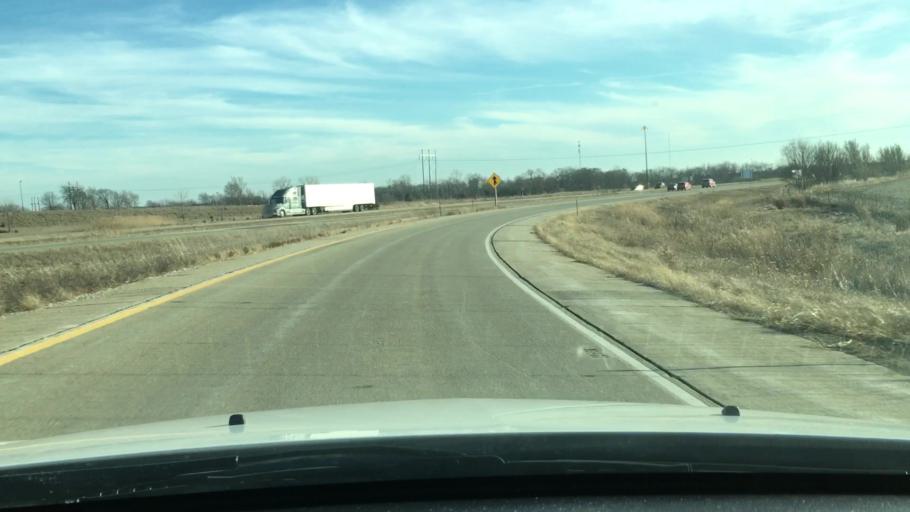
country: US
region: Illinois
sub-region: LaSalle County
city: Oglesby
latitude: 41.2748
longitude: -89.0824
